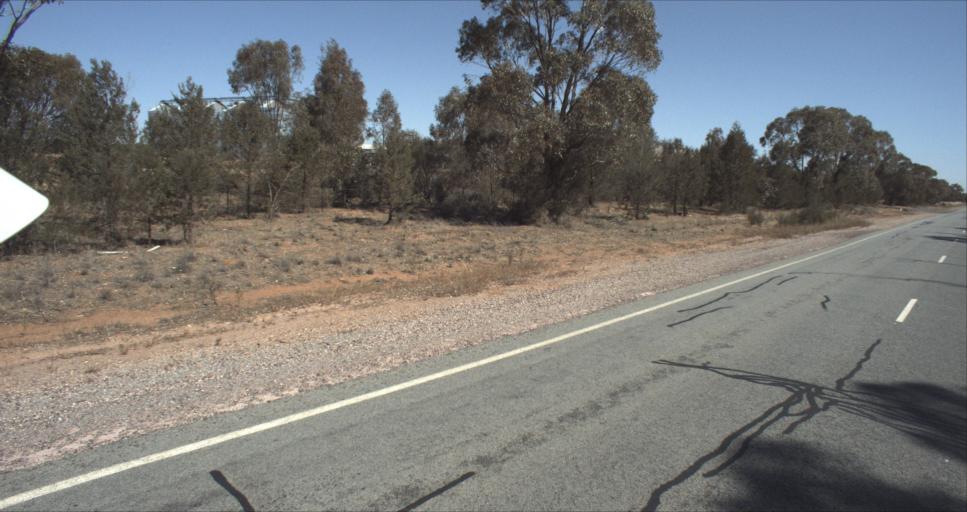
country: AU
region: New South Wales
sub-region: Leeton
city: Leeton
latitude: -34.4968
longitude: 146.4549
